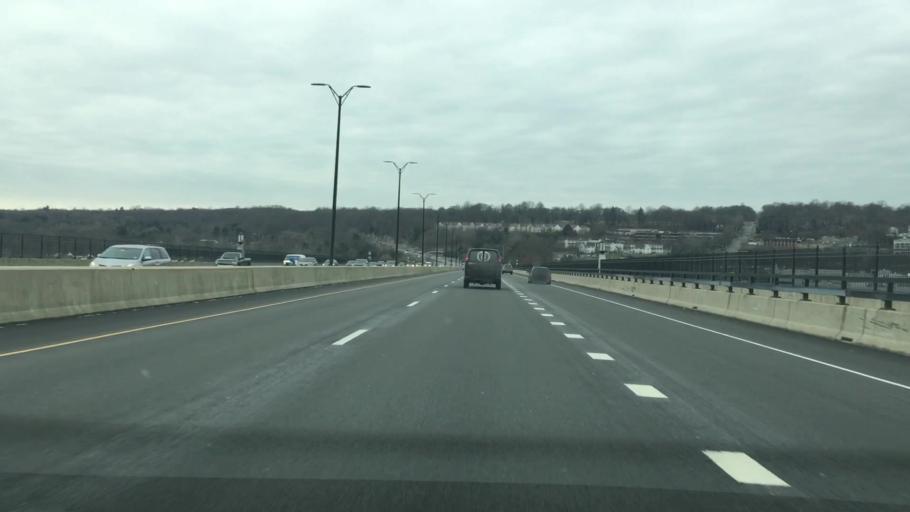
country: US
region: Connecticut
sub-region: New Haven County
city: City of Milford (balance)
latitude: 41.2470
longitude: -73.0910
